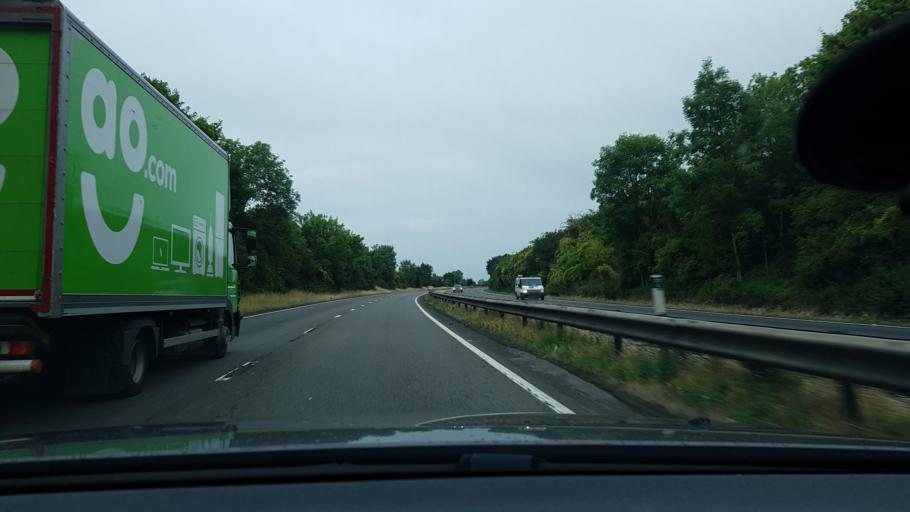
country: GB
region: England
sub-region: Hampshire
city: Overton
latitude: 51.2430
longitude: -1.3415
